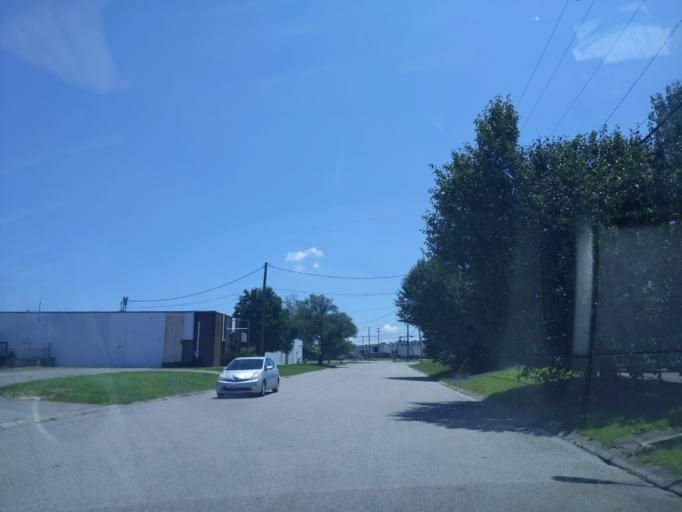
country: US
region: Tennessee
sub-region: Davidson County
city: Nashville
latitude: 36.1393
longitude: -86.7446
